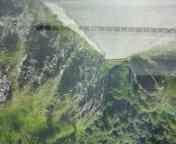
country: IT
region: Lombardy
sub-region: Provincia di Lecco
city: Morterone
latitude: 45.8911
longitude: 9.4575
